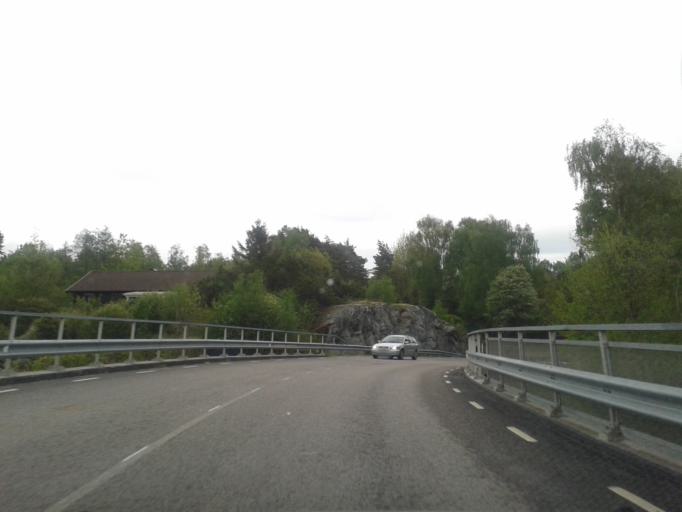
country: SE
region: Vaestra Goetaland
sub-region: Kungalvs Kommun
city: Kode
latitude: 57.9106
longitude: 11.8888
